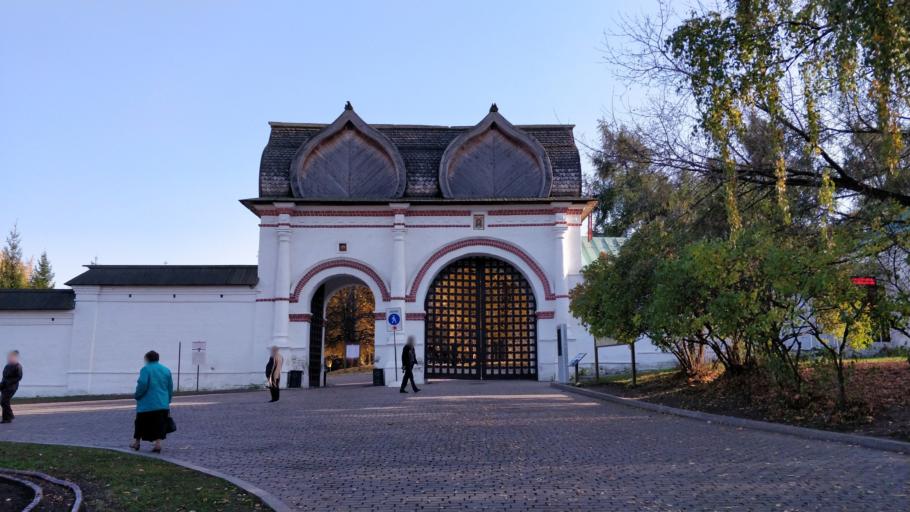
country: RU
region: Moscow
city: Kolomenskoye
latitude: 55.6696
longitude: 37.6657
